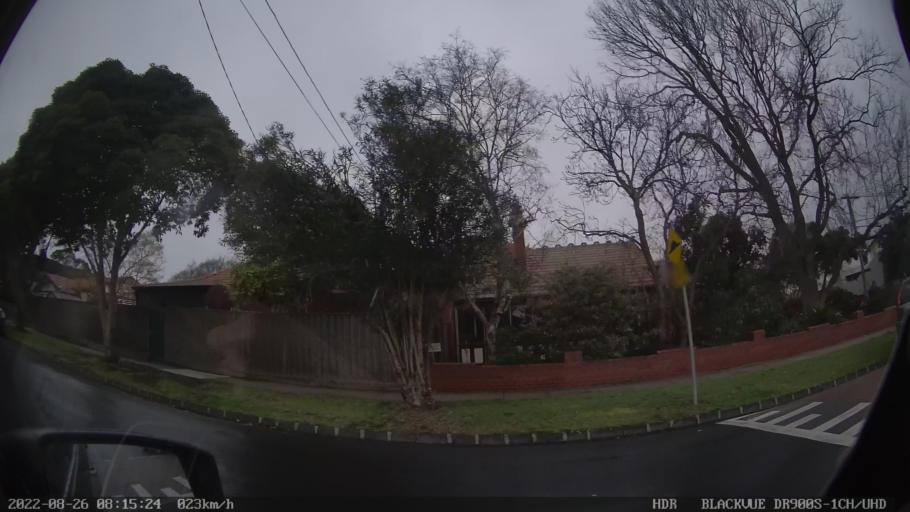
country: AU
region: Victoria
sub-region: Glen Eira
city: Elsternwick
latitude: -37.8930
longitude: 145.0086
